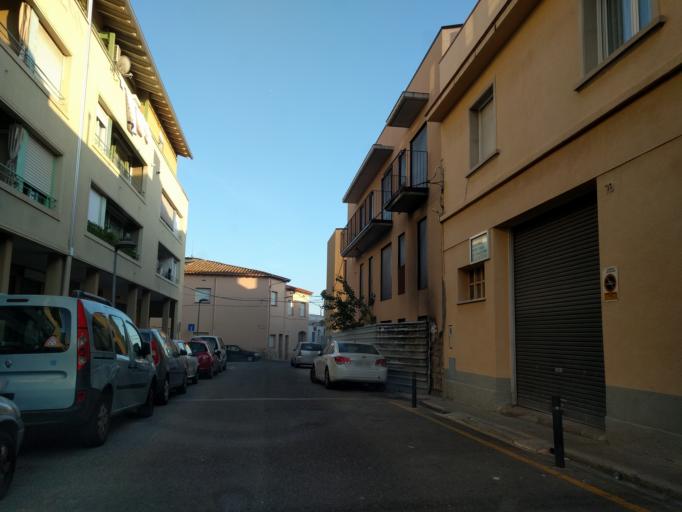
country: ES
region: Catalonia
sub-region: Provincia de Girona
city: Sant Feliu de Guixols
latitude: 41.7855
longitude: 3.0305
